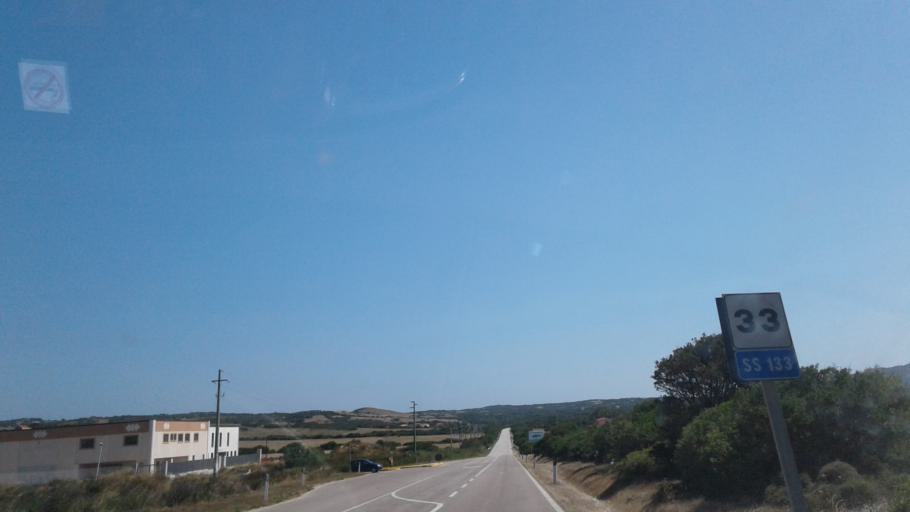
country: IT
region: Sardinia
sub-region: Provincia di Olbia-Tempio
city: Luogosanto
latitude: 41.1182
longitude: 9.2675
